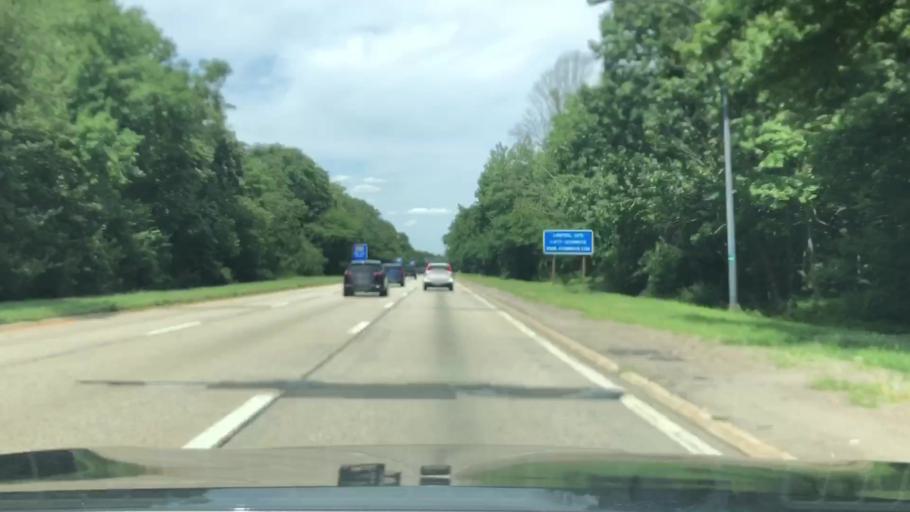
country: US
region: New York
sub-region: Nassau County
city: Freeport
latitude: 40.6711
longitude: -73.5694
